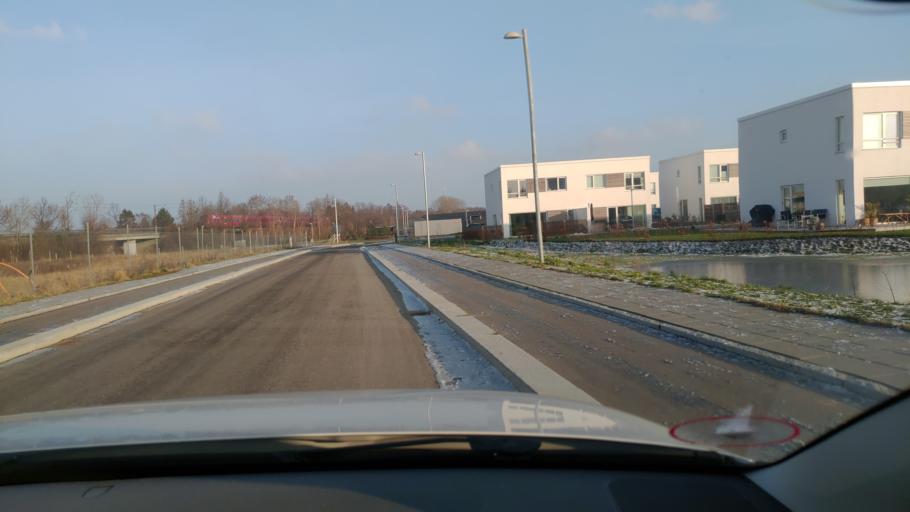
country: DK
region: Zealand
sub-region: Solrod Kommune
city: Solrod Strand
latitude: 55.5457
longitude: 12.2352
